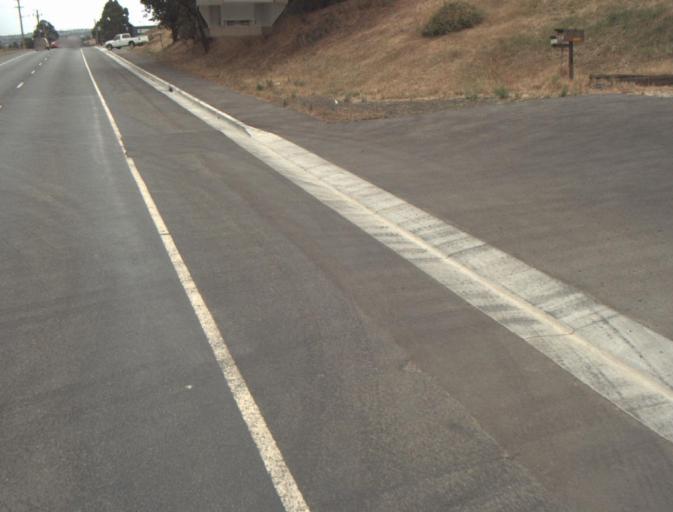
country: AU
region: Tasmania
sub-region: Launceston
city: Newstead
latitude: -41.4433
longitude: 147.1822
